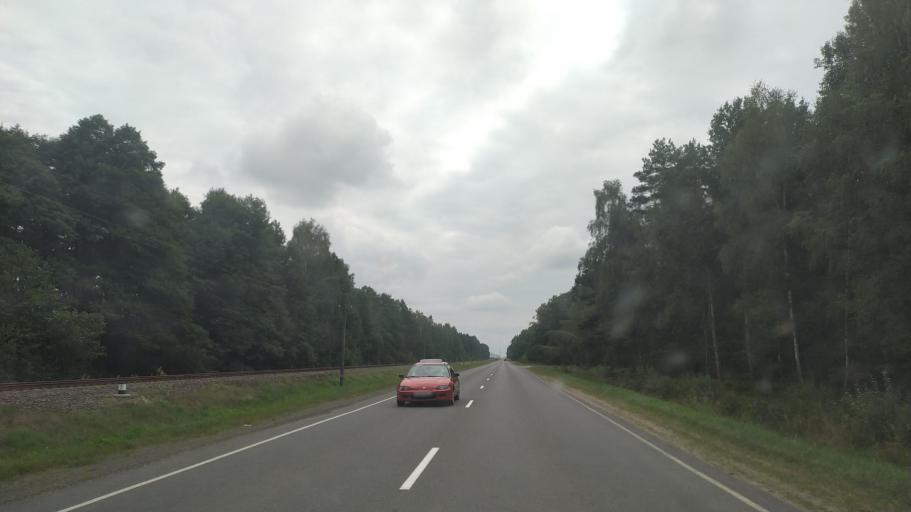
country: BY
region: Brest
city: Byelaazyorsk
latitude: 52.5332
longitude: 25.1426
